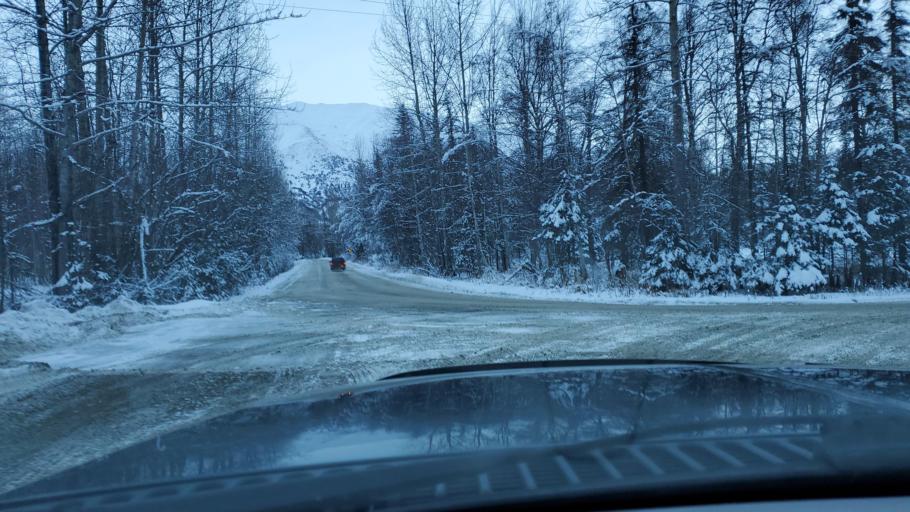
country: US
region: Alaska
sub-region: Matanuska-Susitna Borough
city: Fishhook
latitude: 61.6910
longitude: -149.2998
